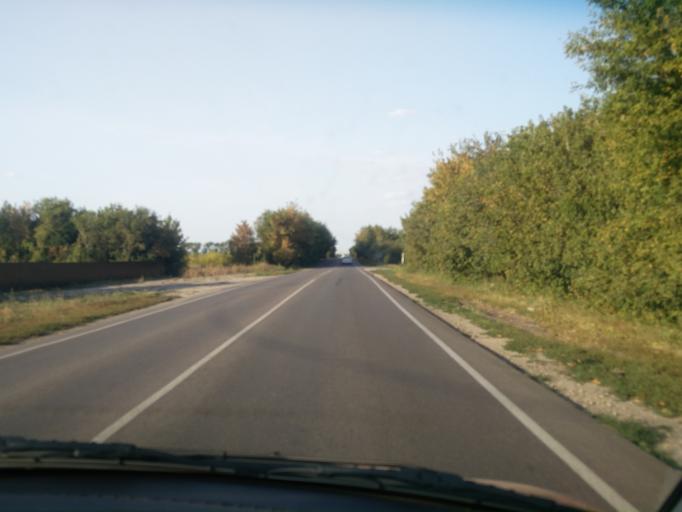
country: RU
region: Voronezj
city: Ramon'
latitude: 51.9195
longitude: 39.3210
